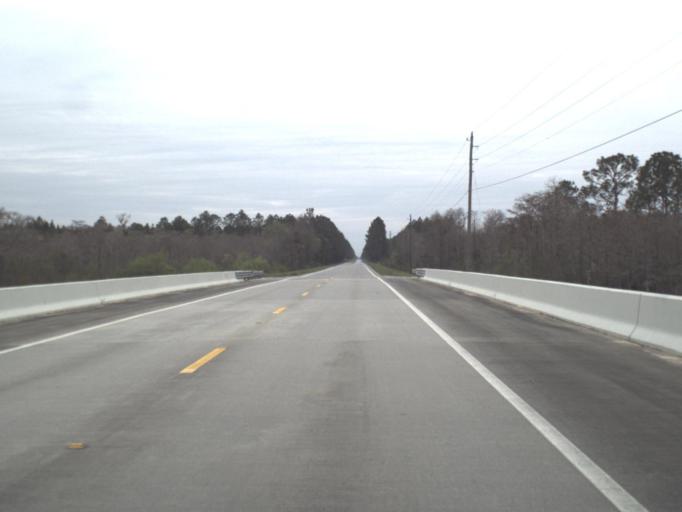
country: US
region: Florida
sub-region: Gulf County
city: Wewahitchka
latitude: 29.9465
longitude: -85.1841
